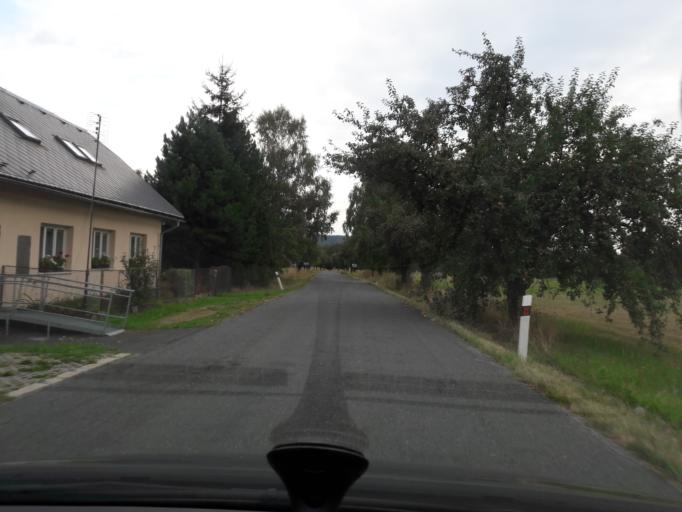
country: CZ
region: Olomoucky
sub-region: Okres Sumperk
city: Loucna nad Desnou
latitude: 50.0595
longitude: 17.0848
